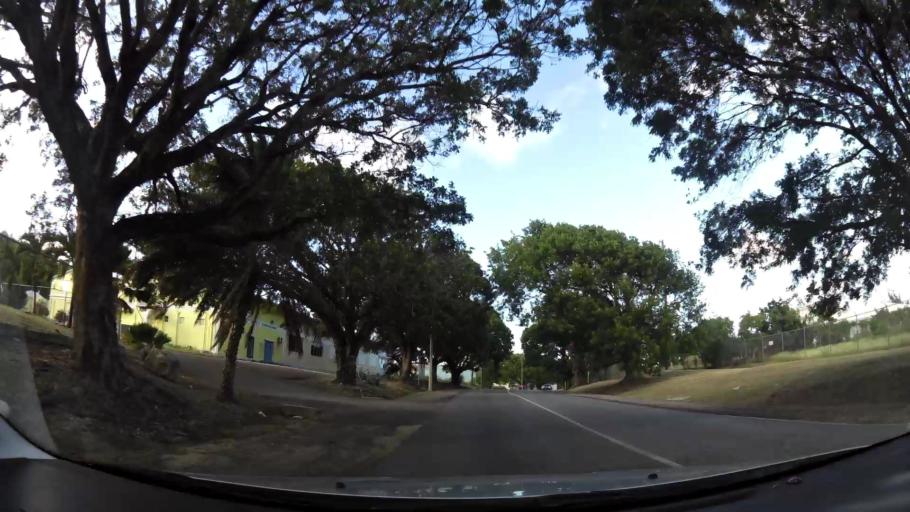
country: AG
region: Saint George
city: Piggotts
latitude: 17.1386
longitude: -61.7977
